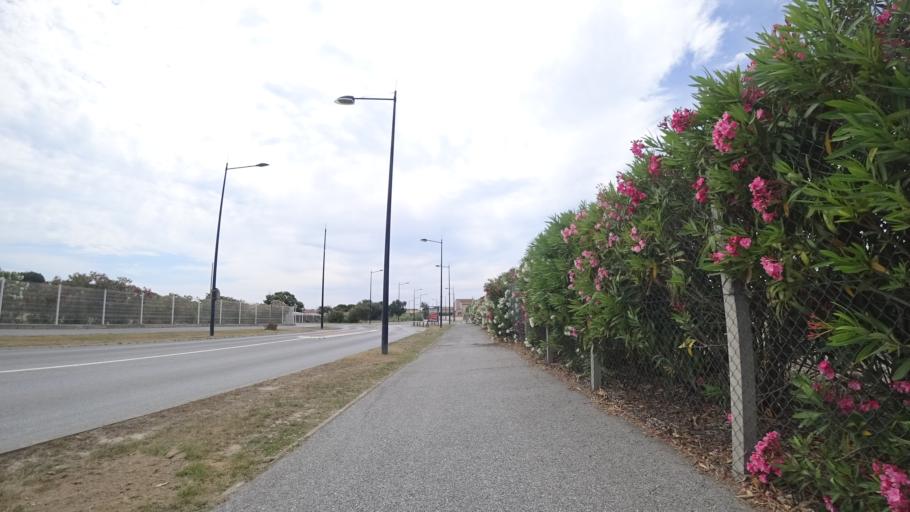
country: FR
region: Languedoc-Roussillon
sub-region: Departement des Pyrenees-Orientales
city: Le Barcares
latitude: 42.7965
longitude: 3.0305
